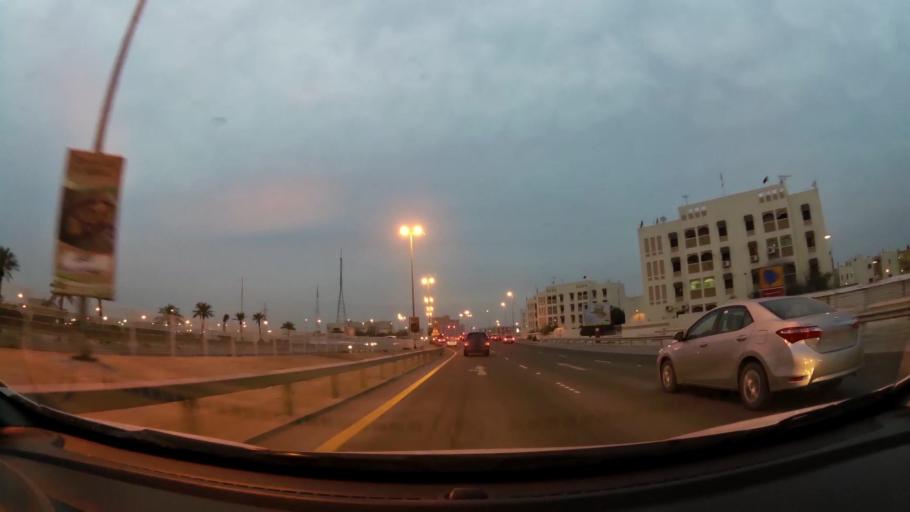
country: BH
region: Northern
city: Madinat `Isa
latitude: 26.1600
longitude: 50.5645
